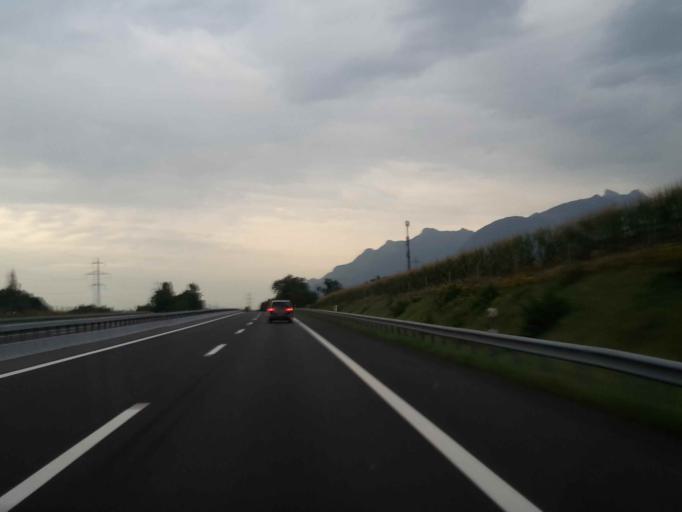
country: CH
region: Vaud
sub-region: Aigle District
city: Bex
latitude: 46.2413
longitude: 6.9966
